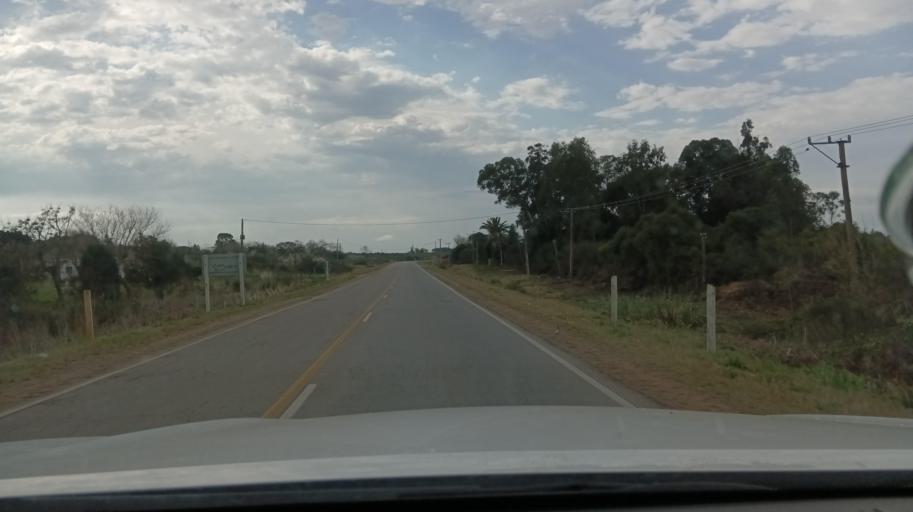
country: UY
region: Canelones
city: Toledo
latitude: -34.7139
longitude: -56.1121
